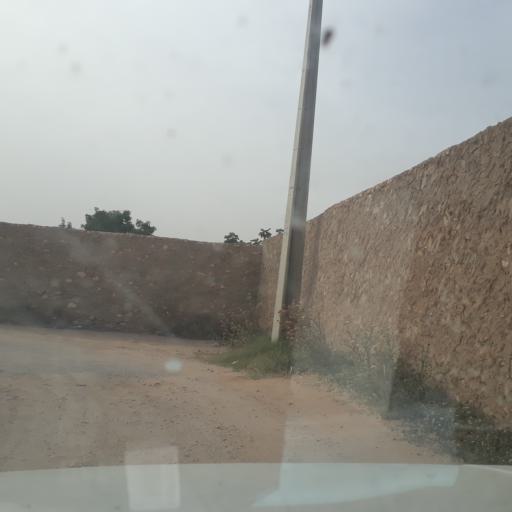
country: TN
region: Safaqis
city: Al Qarmadah
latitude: 34.8223
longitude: 10.7769
